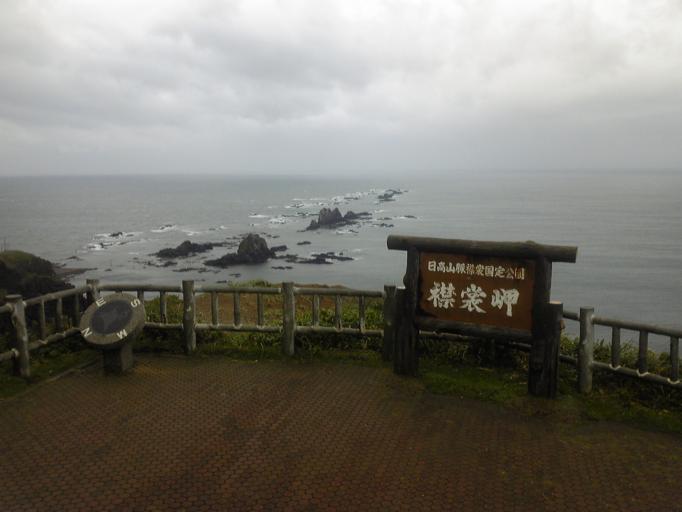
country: JP
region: Hokkaido
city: Shizunai-furukawacho
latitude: 41.9274
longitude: 143.2438
